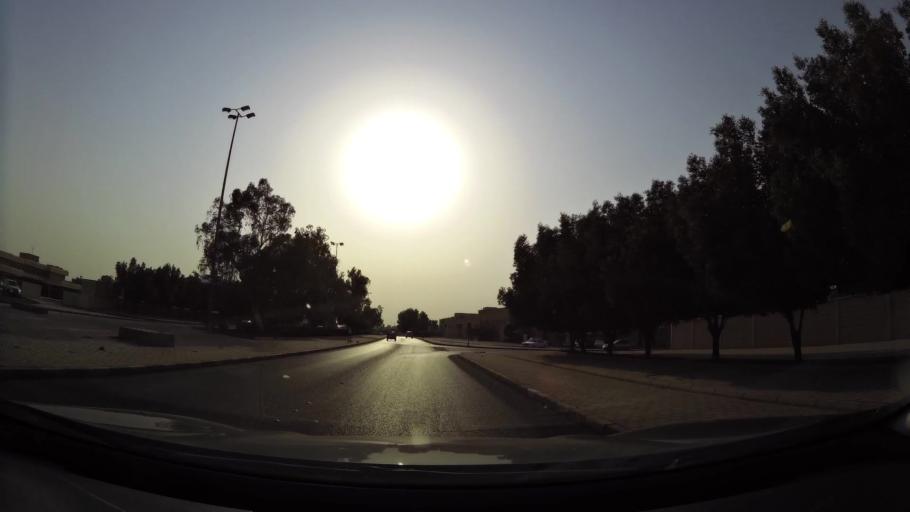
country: KW
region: Muhafazat Hawalli
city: Ar Rumaythiyah
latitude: 29.3149
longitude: 48.0660
